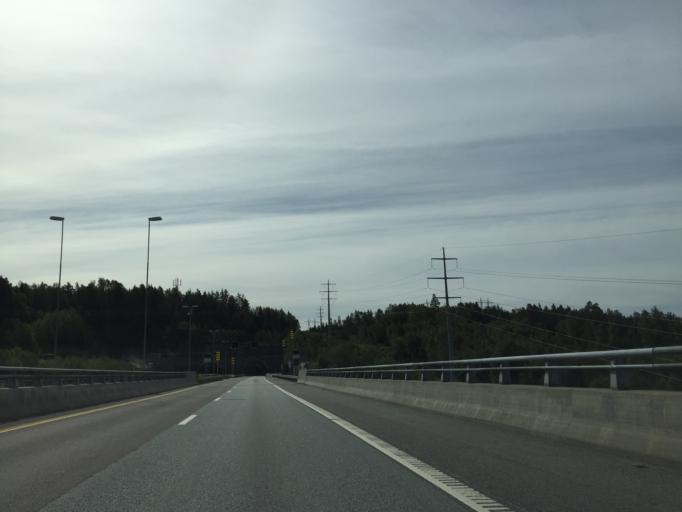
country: NO
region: Akershus
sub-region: Vestby
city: Vestby
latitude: 59.5378
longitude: 10.7269
